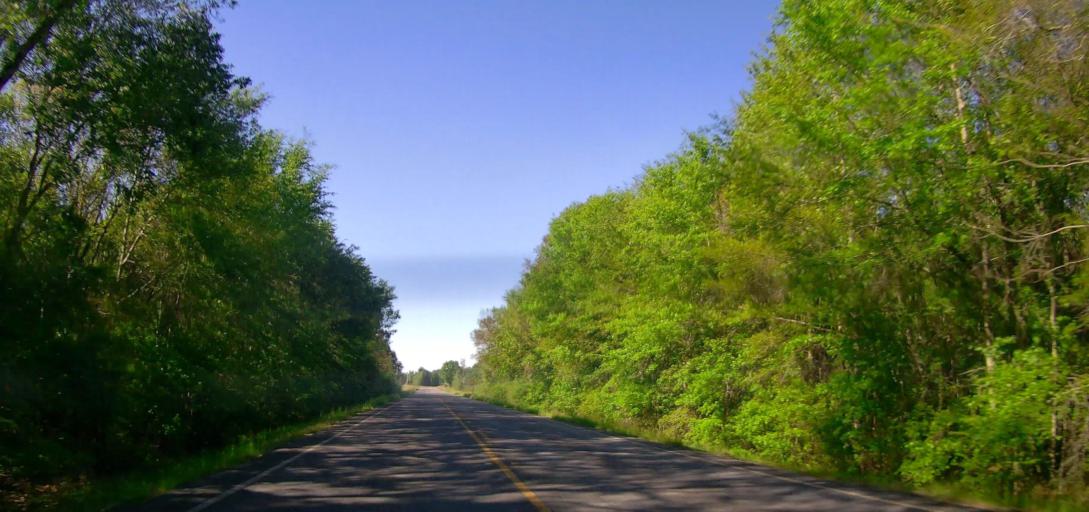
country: US
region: Georgia
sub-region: Wilcox County
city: Rochelle
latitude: 32.0935
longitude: -83.5032
